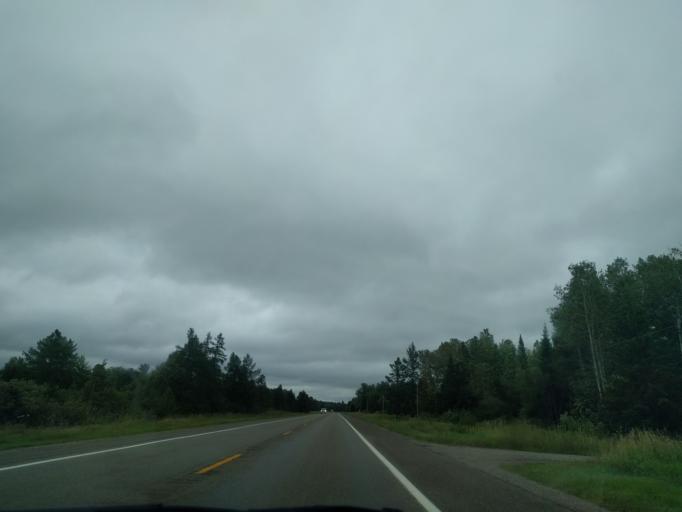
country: US
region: Michigan
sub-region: Marquette County
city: K. I. Sawyer Air Force Base
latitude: 46.2817
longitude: -87.3270
